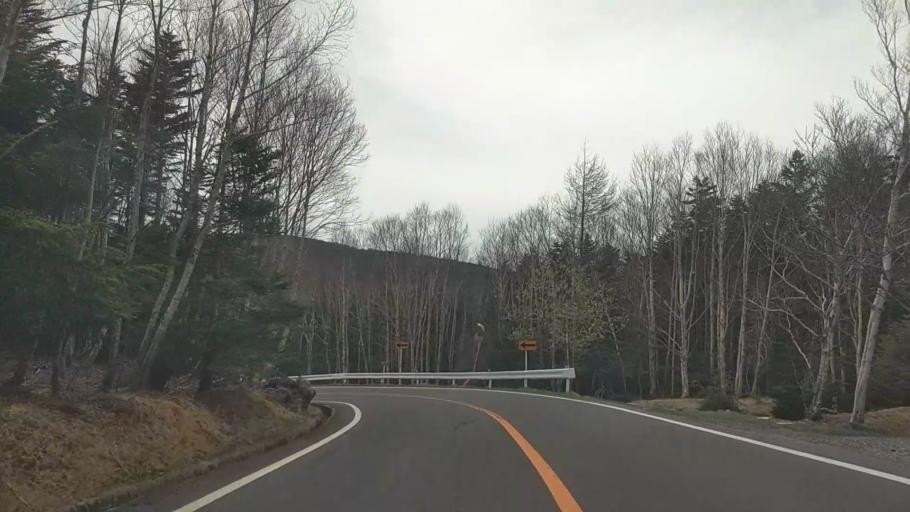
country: JP
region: Nagano
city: Saku
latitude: 36.0595
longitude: 138.3610
